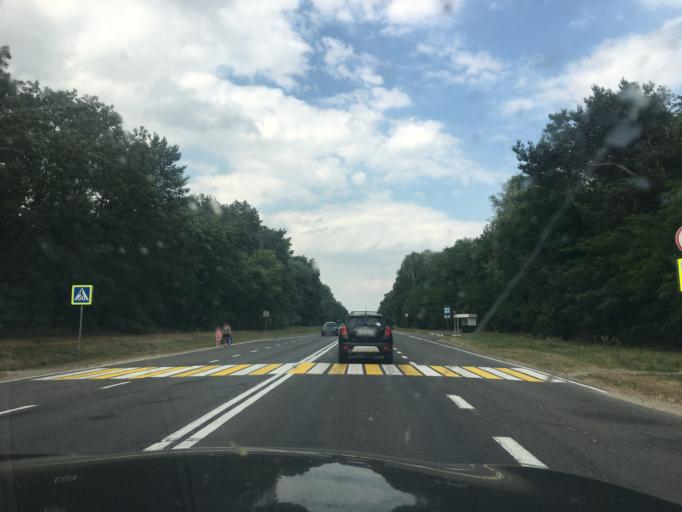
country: BY
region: Brest
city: Charnawchytsy
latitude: 52.1674
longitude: 23.7049
